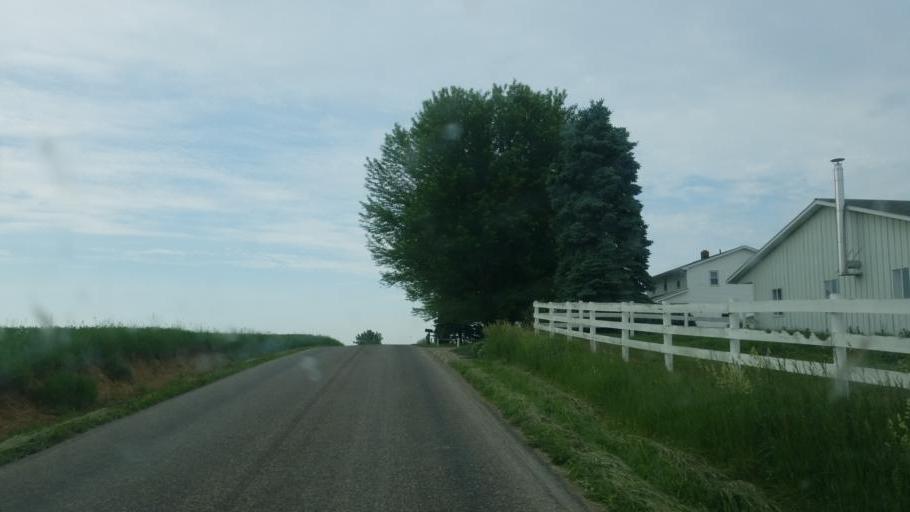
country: US
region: Ohio
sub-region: Wayne County
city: Apple Creek
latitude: 40.6847
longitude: -81.7652
